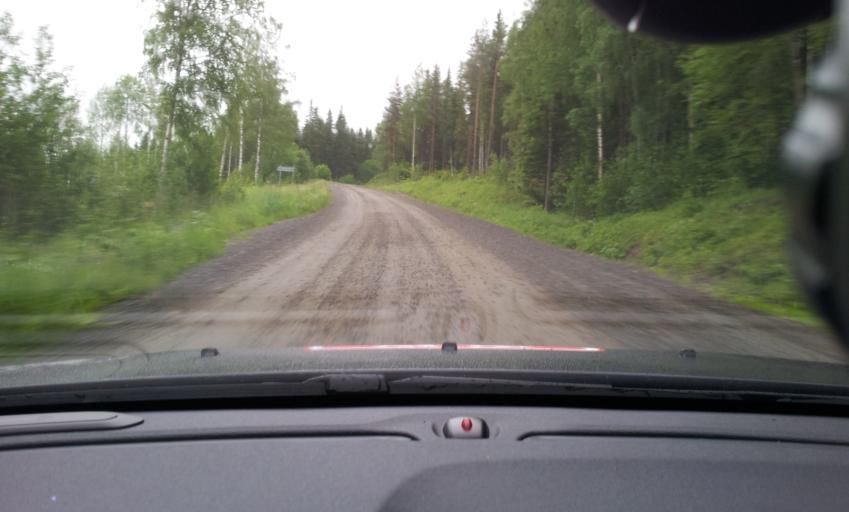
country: SE
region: Jaemtland
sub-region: Ragunda Kommun
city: Hammarstrand
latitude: 63.1369
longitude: 16.1608
